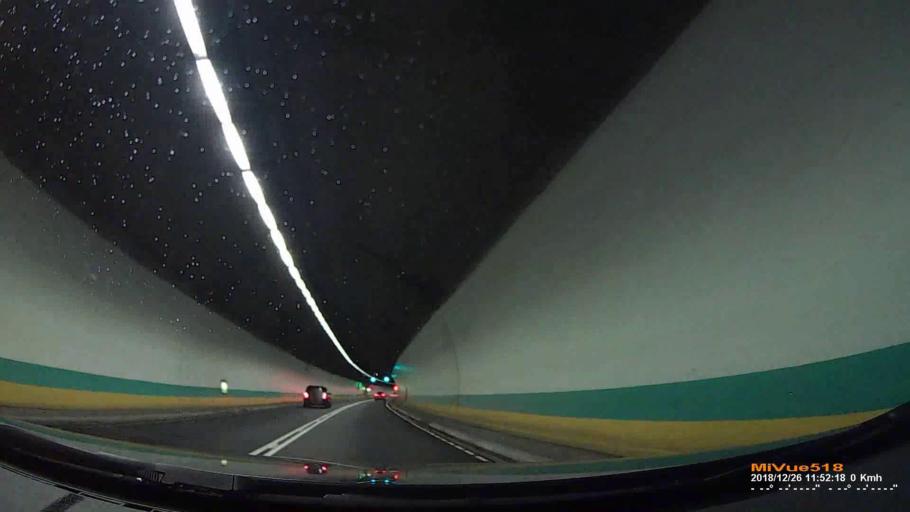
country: TW
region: Taiwan
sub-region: Keelung
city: Keelung
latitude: 24.9679
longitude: 121.6836
